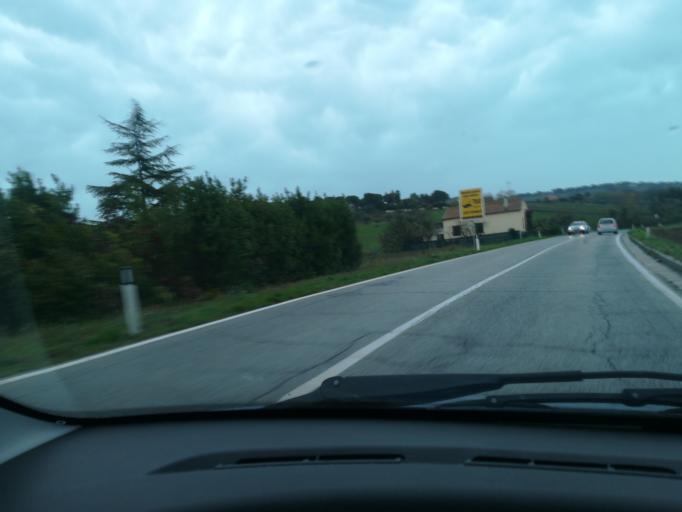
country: IT
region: The Marches
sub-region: Provincia di Macerata
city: Borgo Stazione
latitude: 43.2934
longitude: 13.6640
